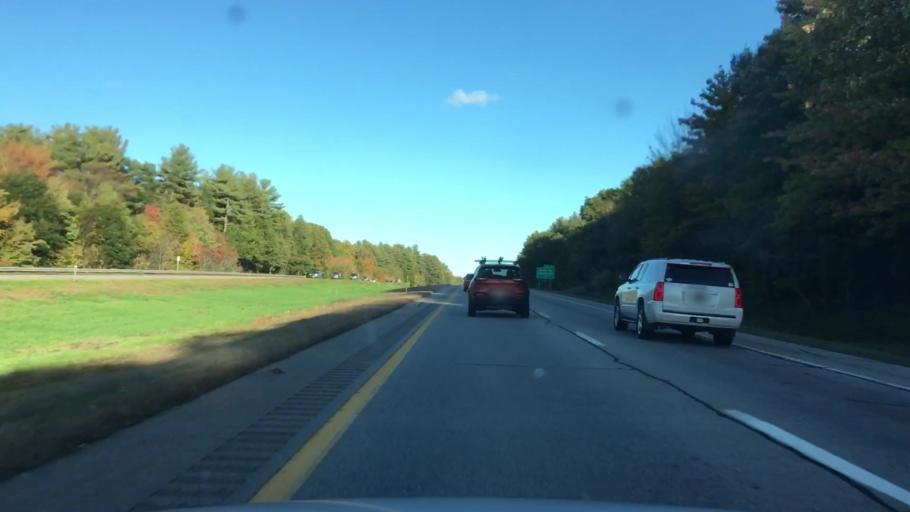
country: US
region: New Hampshire
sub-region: Rockingham County
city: Fremont
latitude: 43.0313
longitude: -71.1400
